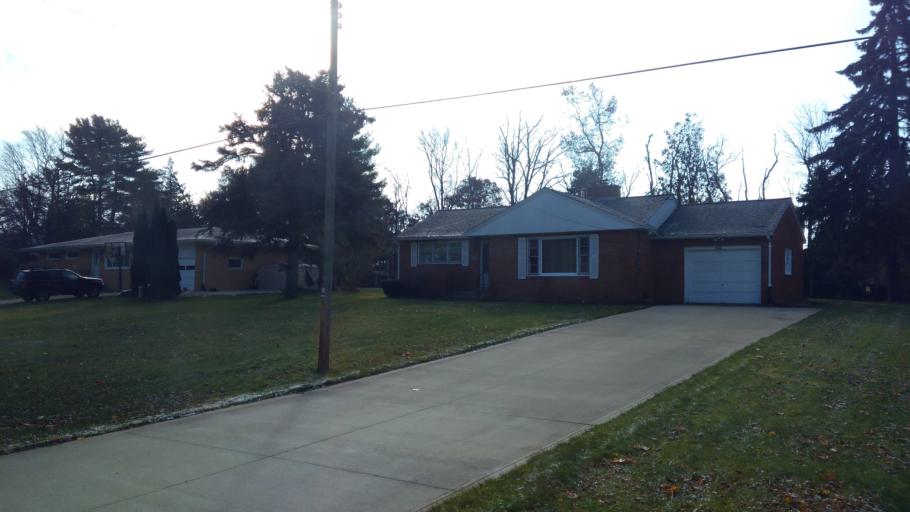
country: US
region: Ohio
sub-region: Richland County
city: Lexington
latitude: 40.7040
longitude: -82.5384
